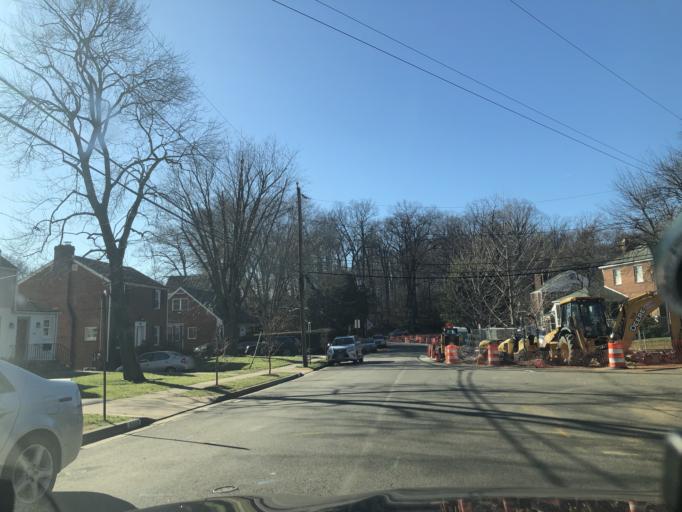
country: US
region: Virginia
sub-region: Arlington County
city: Arlington
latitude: 38.8836
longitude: -77.1229
